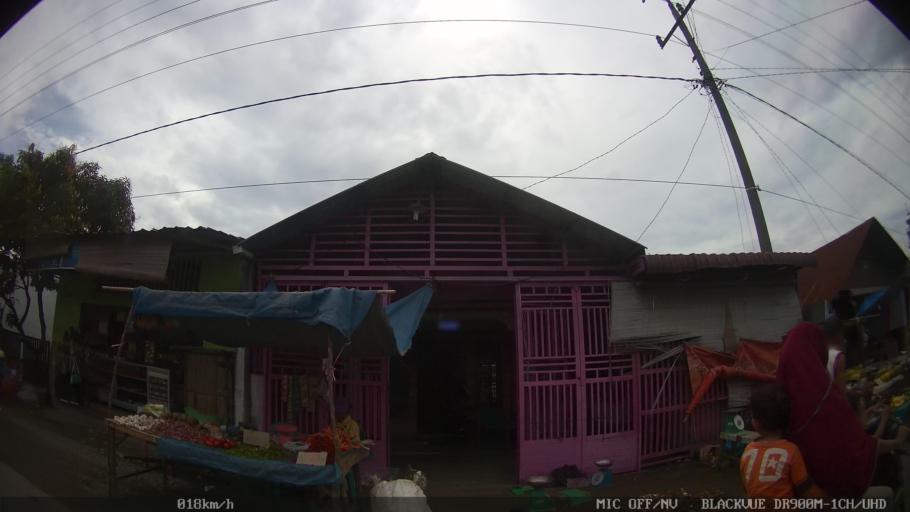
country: ID
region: North Sumatra
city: Sunggal
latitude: 3.6107
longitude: 98.5802
